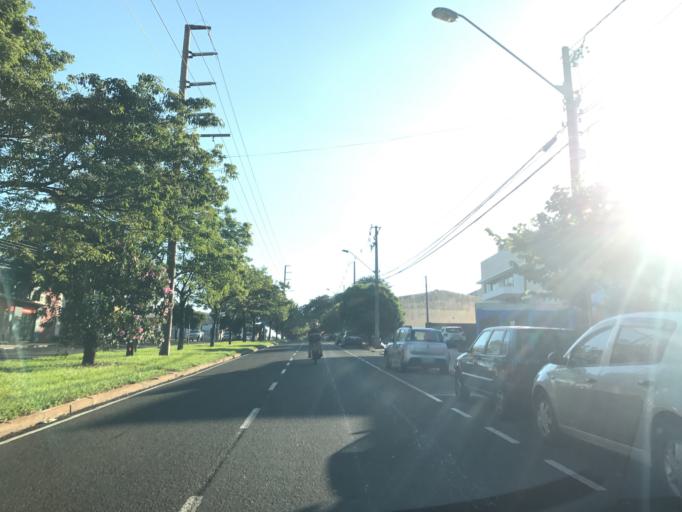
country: BR
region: Parana
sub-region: Maringa
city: Maringa
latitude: -23.4486
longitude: -51.9477
